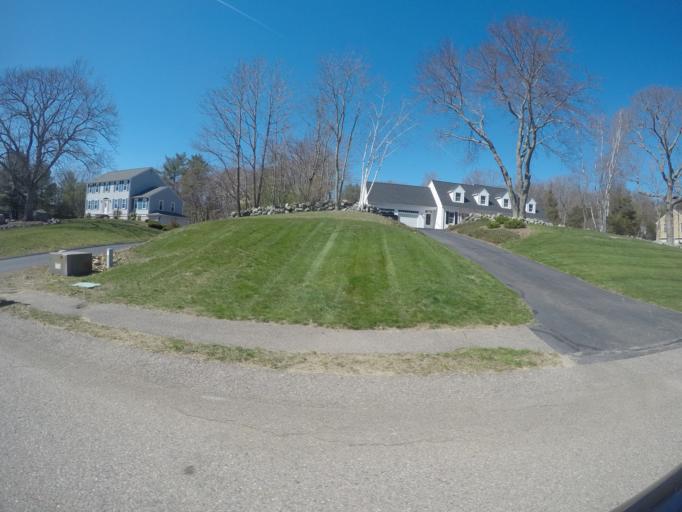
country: US
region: Massachusetts
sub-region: Norfolk County
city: Stoughton
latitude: 42.0858
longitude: -71.0965
